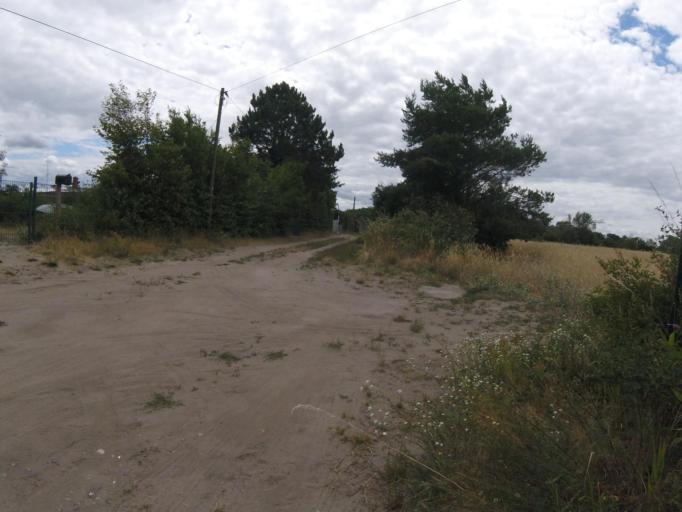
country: DE
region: Brandenburg
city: Mittenwalde
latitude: 52.2577
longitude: 13.5687
